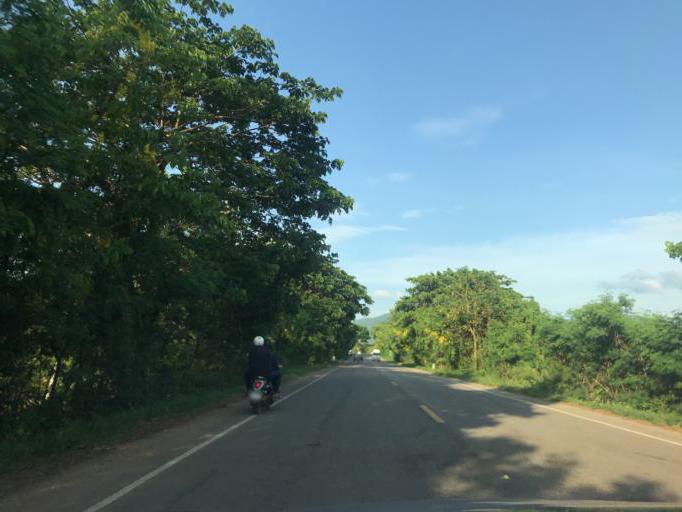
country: TH
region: Phayao
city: Phu Kam Yao
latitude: 19.3133
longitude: 100.0116
